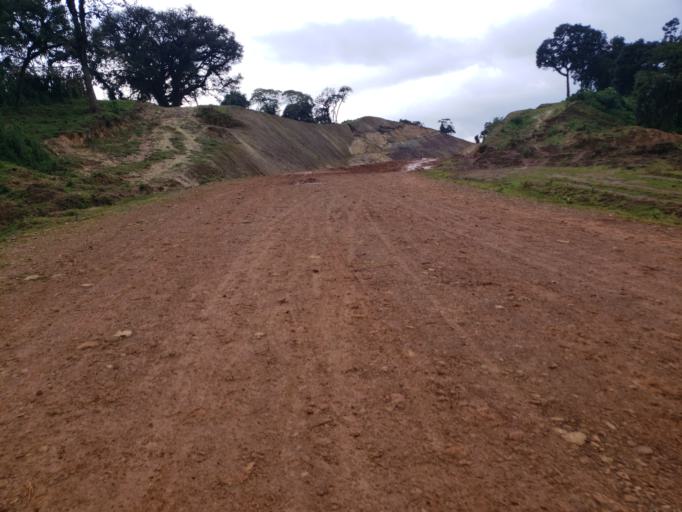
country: ET
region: Oromiya
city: Dodola
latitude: 6.6686
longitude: 39.3660
